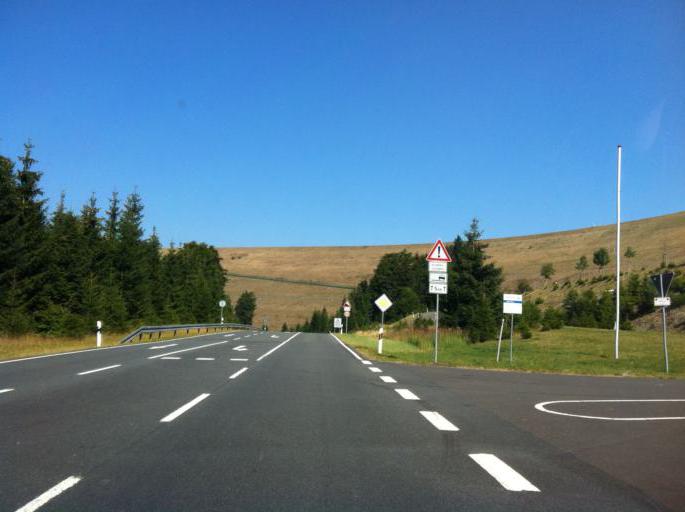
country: DE
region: Thuringia
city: Goldisthal
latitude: 50.5044
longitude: 11.0298
